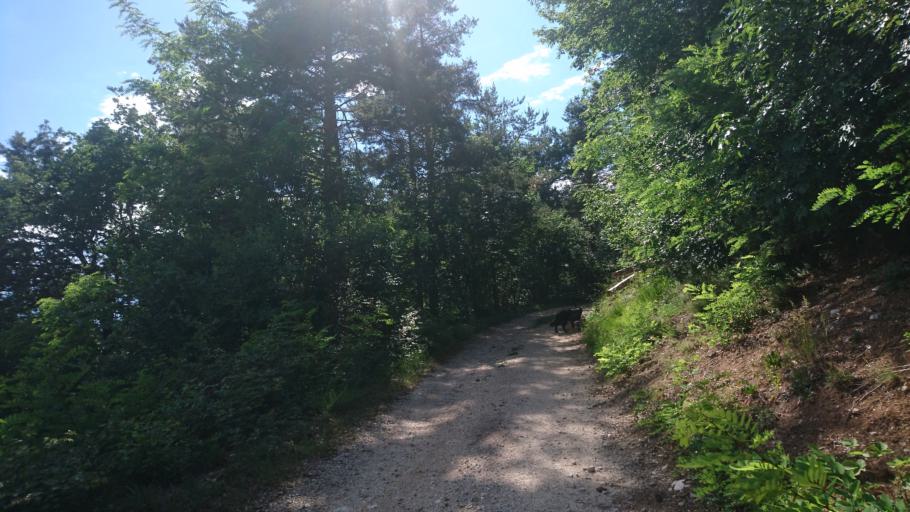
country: IT
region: Trentino-Alto Adige
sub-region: Provincia di Trento
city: Drena
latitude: 45.9722
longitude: 10.9602
